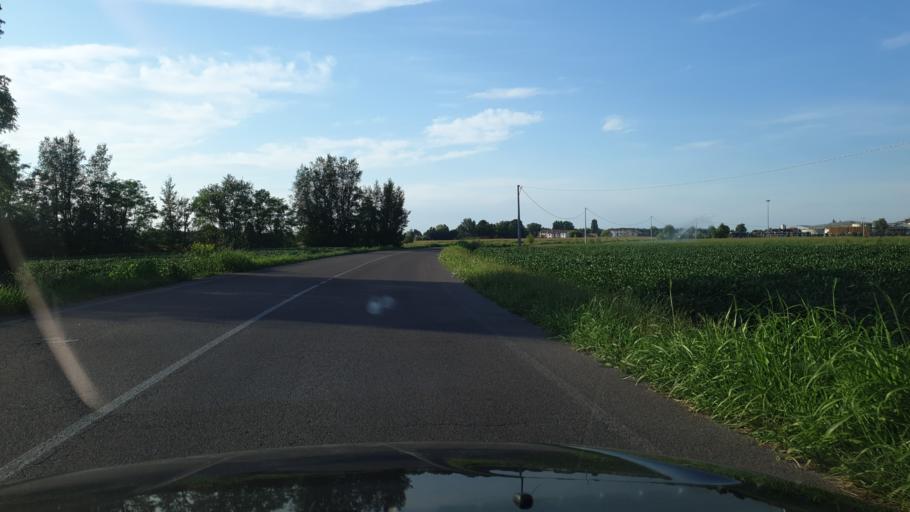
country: IT
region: Veneto
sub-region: Provincia di Rovigo
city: Fiesso Umbertiano
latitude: 44.9543
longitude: 11.6166
